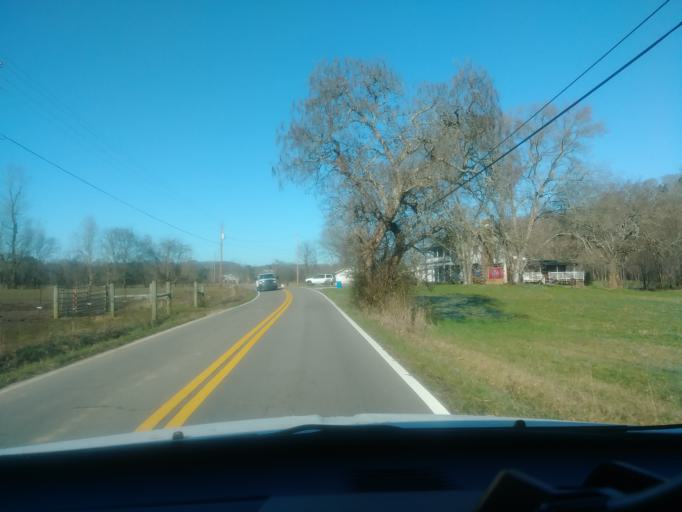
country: US
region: Tennessee
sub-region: Greene County
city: Mosheim
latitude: 36.1179
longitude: -83.0323
